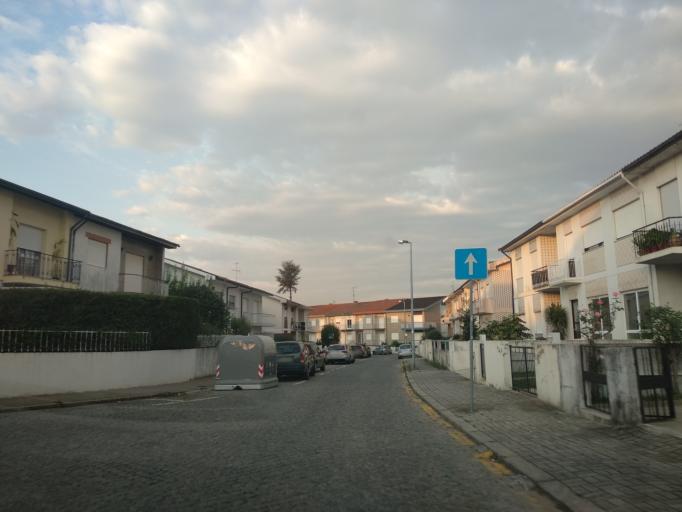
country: PT
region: Braga
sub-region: Braga
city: Braga
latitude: 41.5330
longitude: -8.4404
